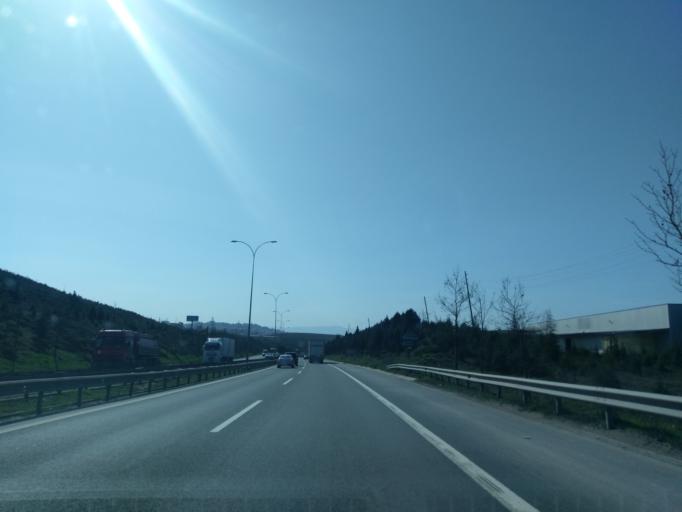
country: TR
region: Kocaeli
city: Balcik
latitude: 40.8506
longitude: 29.3747
